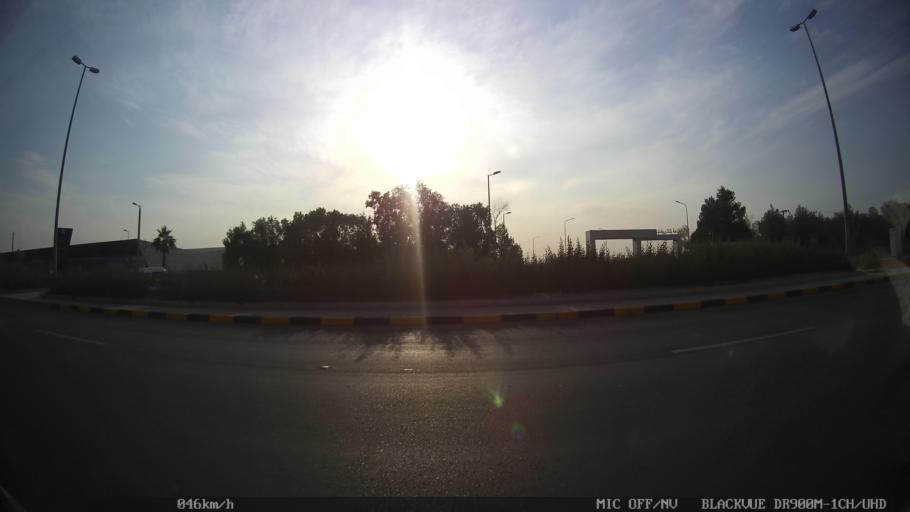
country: KW
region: Al Farwaniyah
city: Janub as Surrah
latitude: 29.2540
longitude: 47.9620
